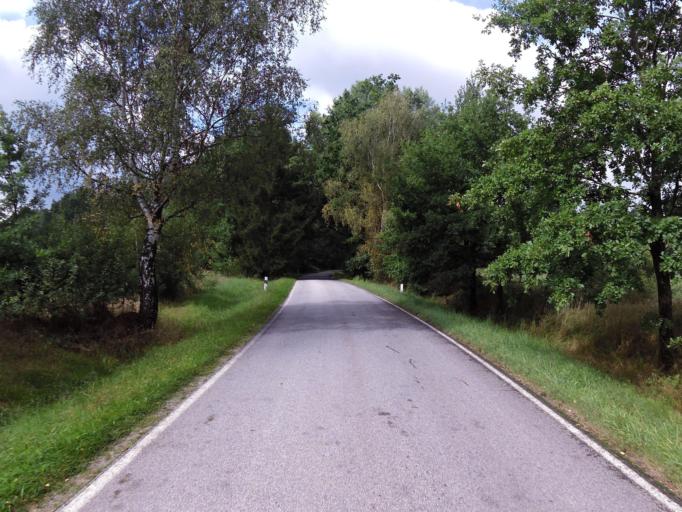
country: CZ
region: Jihocesky
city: Suchdol nad Luznici
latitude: 48.8651
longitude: 14.8608
